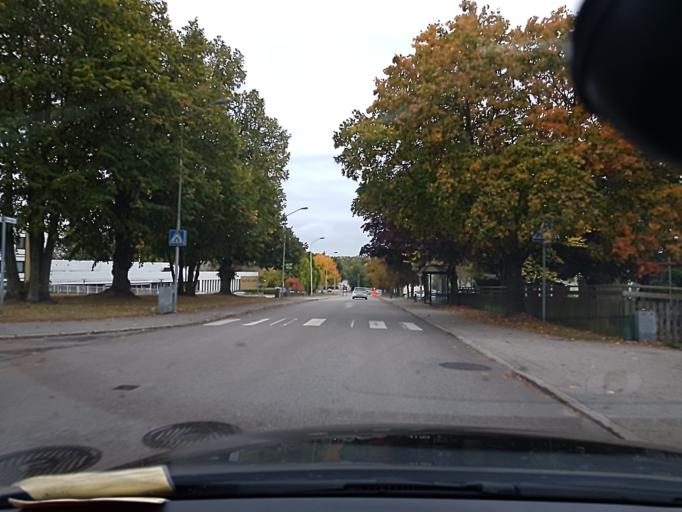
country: SE
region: Kronoberg
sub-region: Vaxjo Kommun
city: Vaexjoe
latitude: 56.8919
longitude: 14.8028
